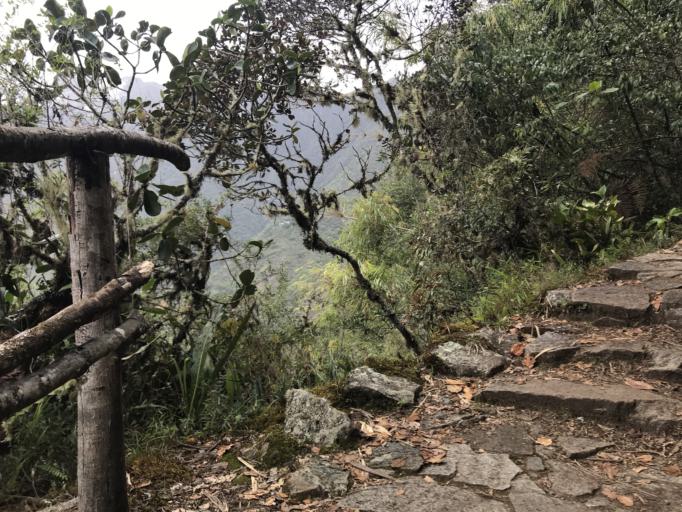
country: PE
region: Cusco
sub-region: Provincia de La Convencion
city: Santa Teresa
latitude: -13.1760
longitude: -72.5360
